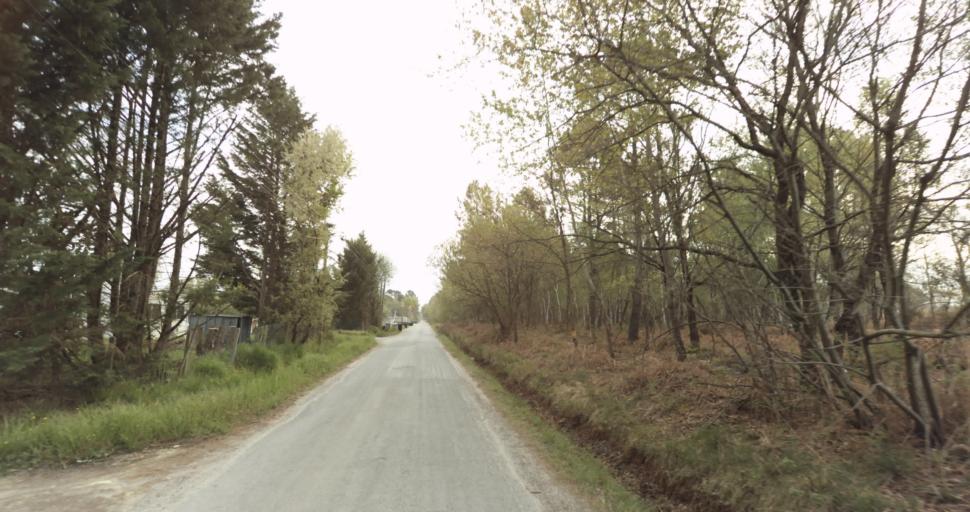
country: FR
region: Aquitaine
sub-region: Departement de la Gironde
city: Saint-Aubin-de-Medoc
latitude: 44.7706
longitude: -0.7439
